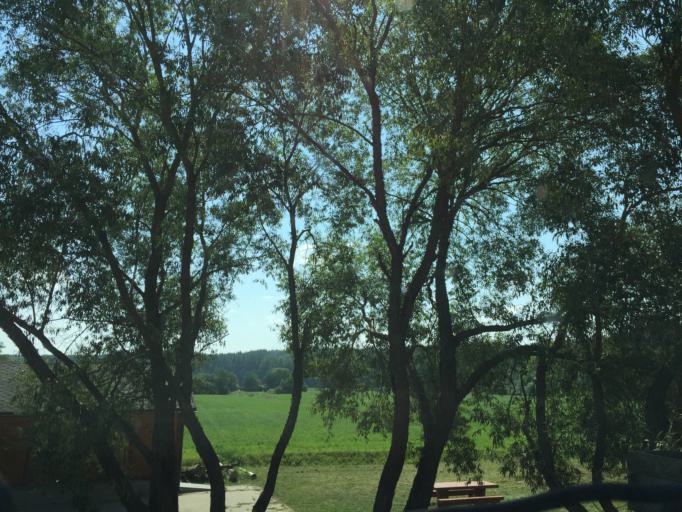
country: LV
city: Tervete
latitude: 56.4971
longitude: 23.4108
